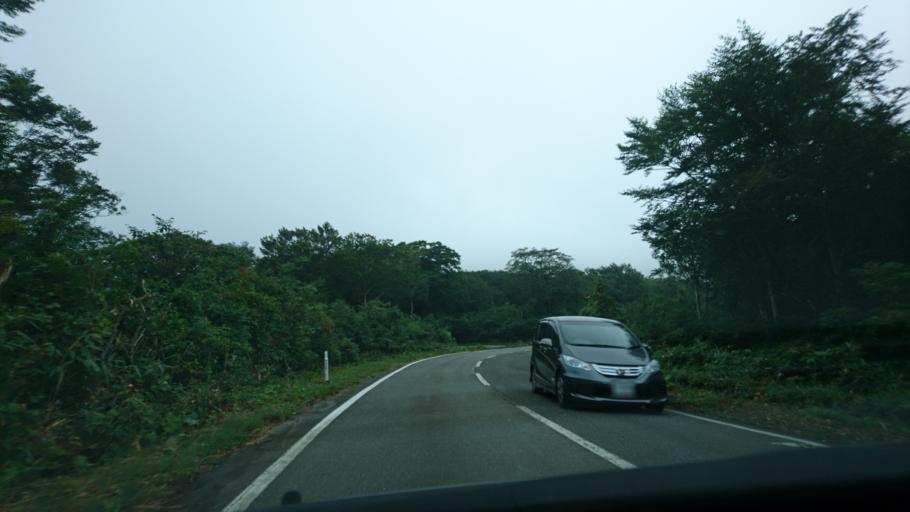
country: JP
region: Akita
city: Yuzawa
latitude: 38.9781
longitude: 140.7551
